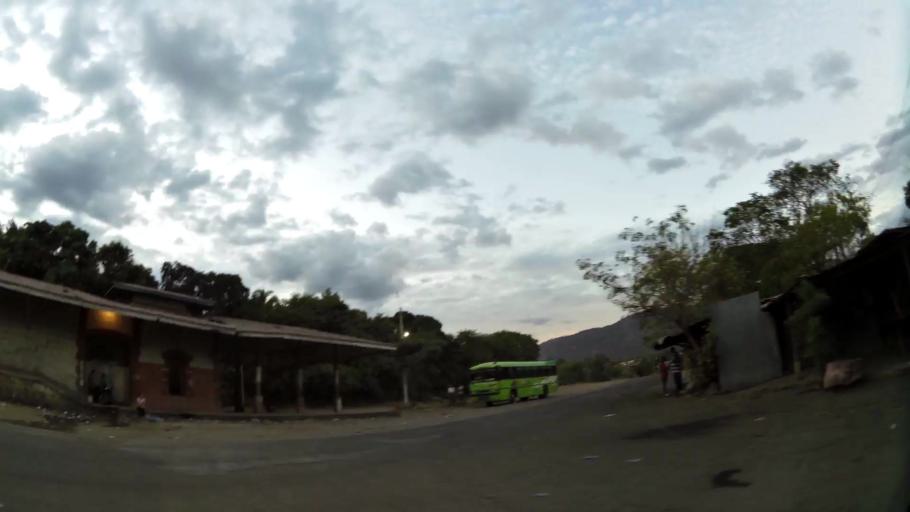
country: SV
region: San Vicente
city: San Vicente
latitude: 13.6428
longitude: -88.7929
